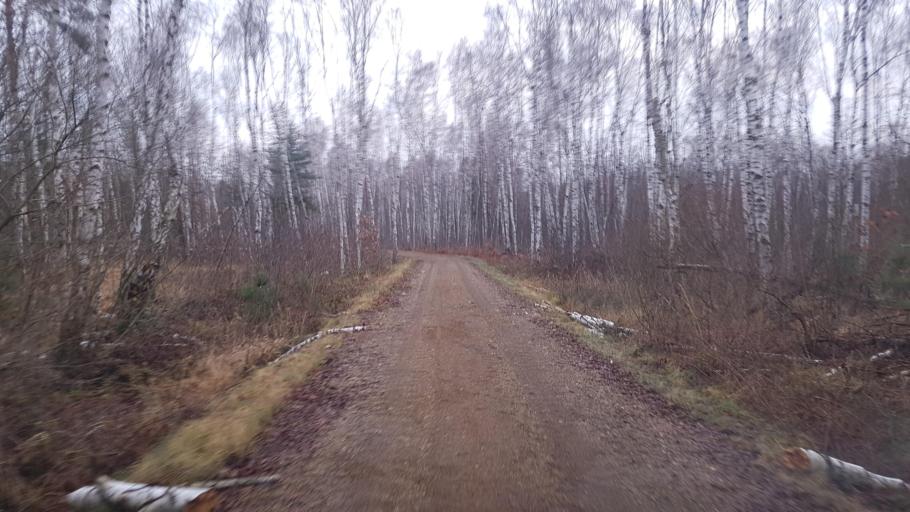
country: DE
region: Brandenburg
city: Plessa
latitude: 51.5209
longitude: 13.6827
